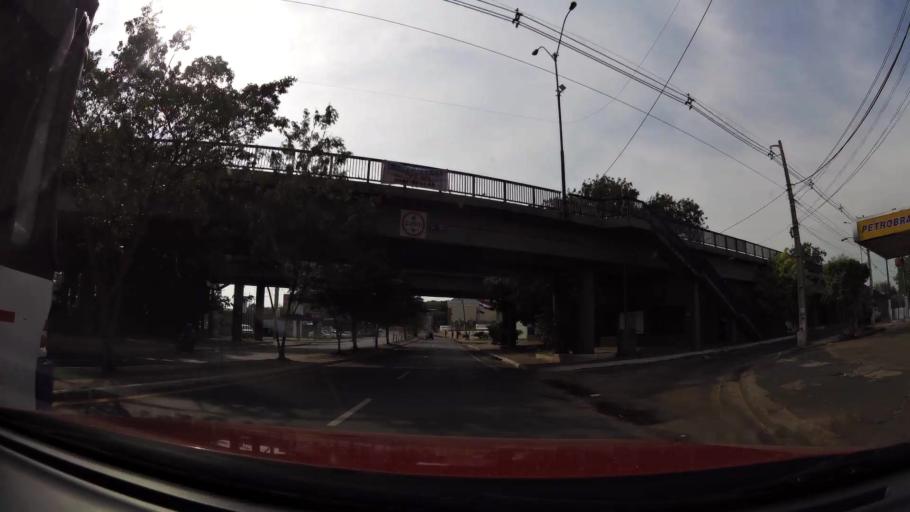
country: PY
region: Central
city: Fernando de la Mora
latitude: -25.3074
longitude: -57.5535
